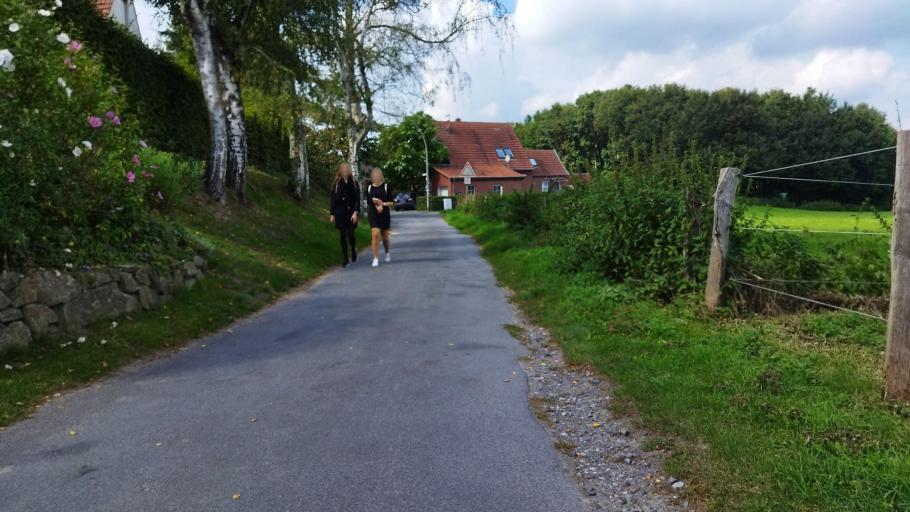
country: DE
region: North Rhine-Westphalia
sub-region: Regierungsbezirk Munster
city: Telgte
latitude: 51.9814
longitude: 7.7975
